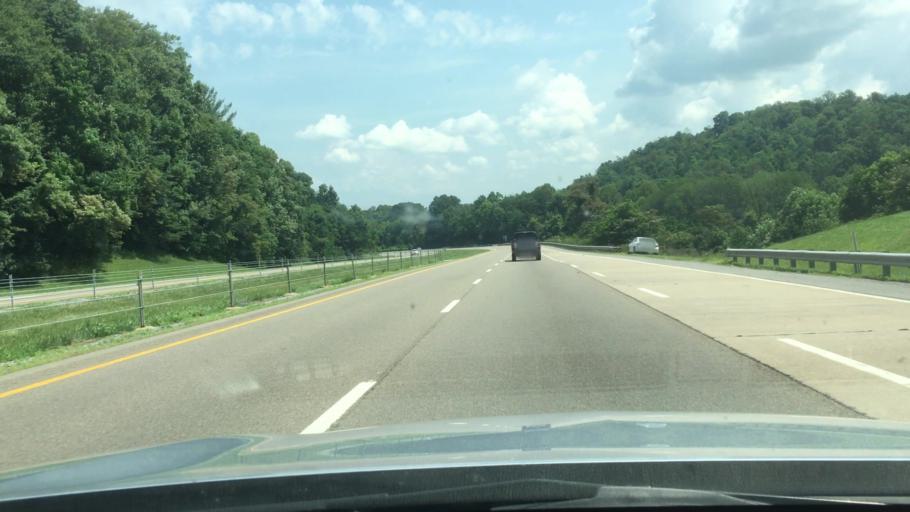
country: US
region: Tennessee
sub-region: Unicoi County
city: Unicoi
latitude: 36.2103
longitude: -82.3499
